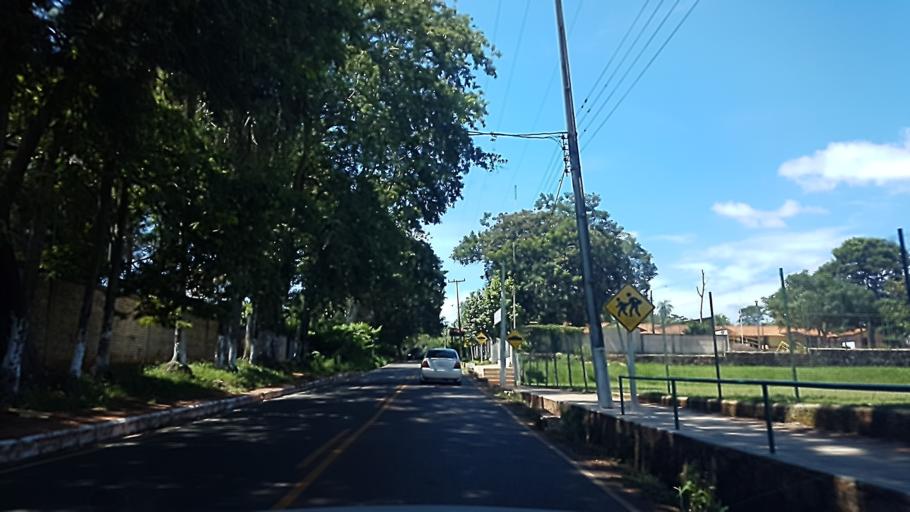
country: PY
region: Central
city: Capiata
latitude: -25.3278
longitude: -57.4407
